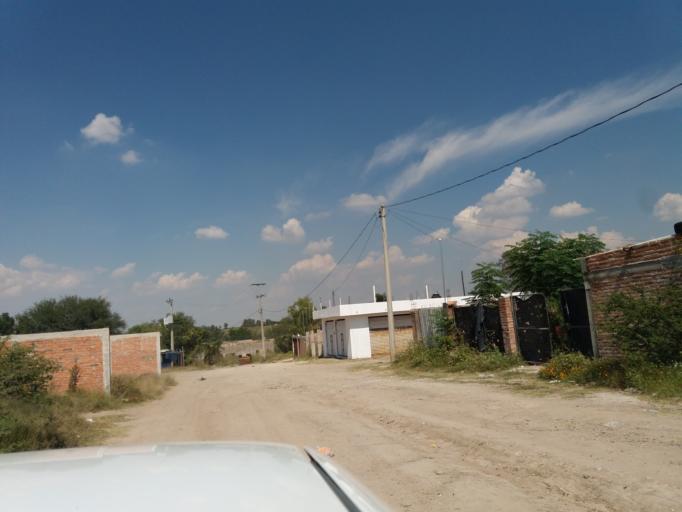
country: MX
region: Aguascalientes
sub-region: Aguascalientes
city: Penuelas (El Cienegal)
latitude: 21.7552
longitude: -102.3015
